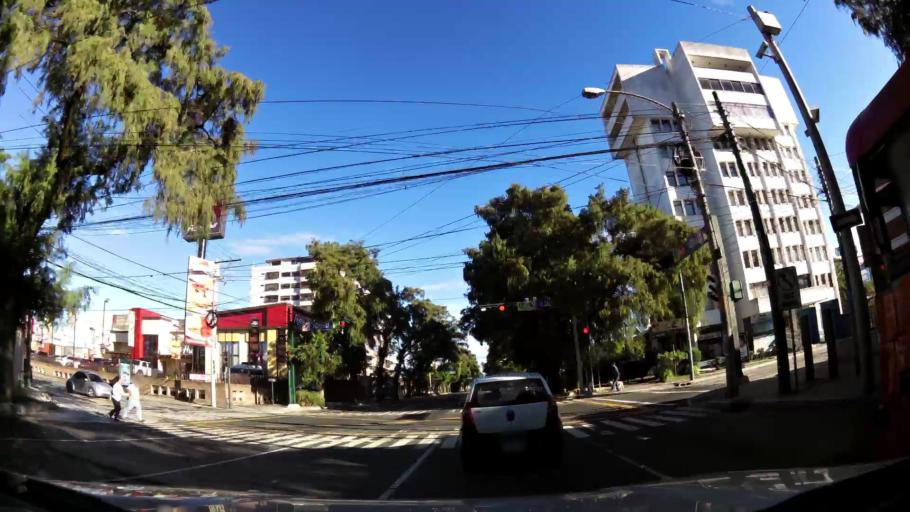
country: GT
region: Guatemala
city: Santa Catarina Pinula
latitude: 14.5981
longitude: -90.5194
